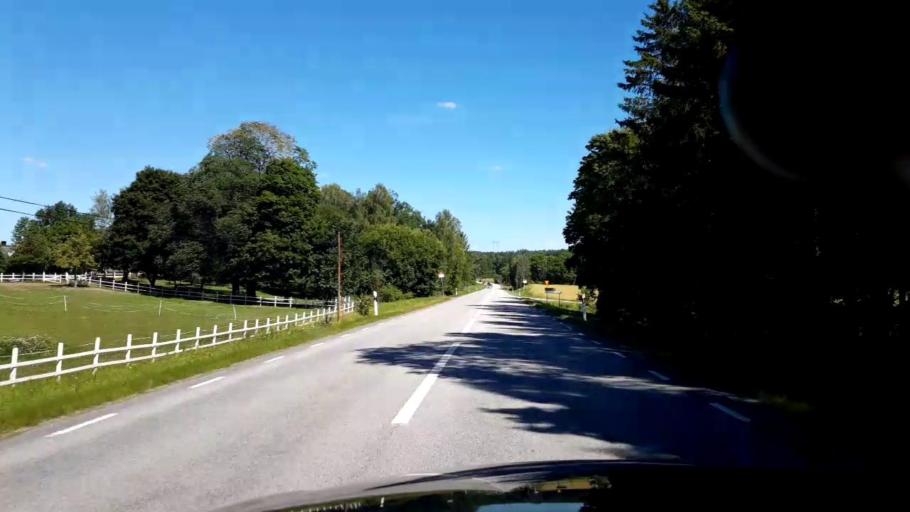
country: SE
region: Uppsala
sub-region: Habo Kommun
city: Balsta
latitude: 59.6349
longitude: 17.6053
